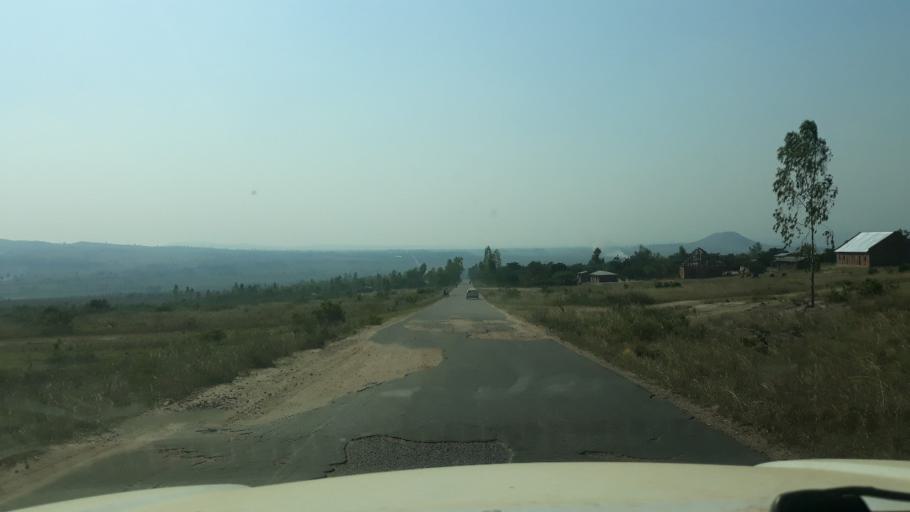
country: BI
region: Cibitoke
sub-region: Commune of Buganda
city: Buganda
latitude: -2.9881
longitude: 29.0925
